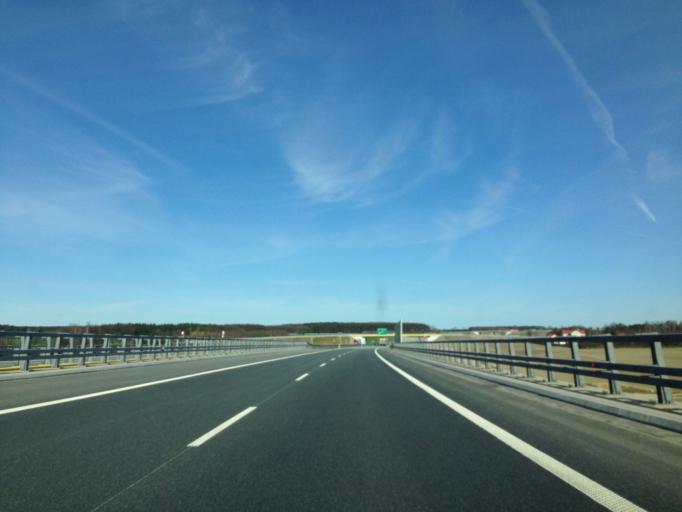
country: PL
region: Lodz Voivodeship
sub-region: Powiat sieradzki
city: Sieradz
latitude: 51.5867
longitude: 18.8067
